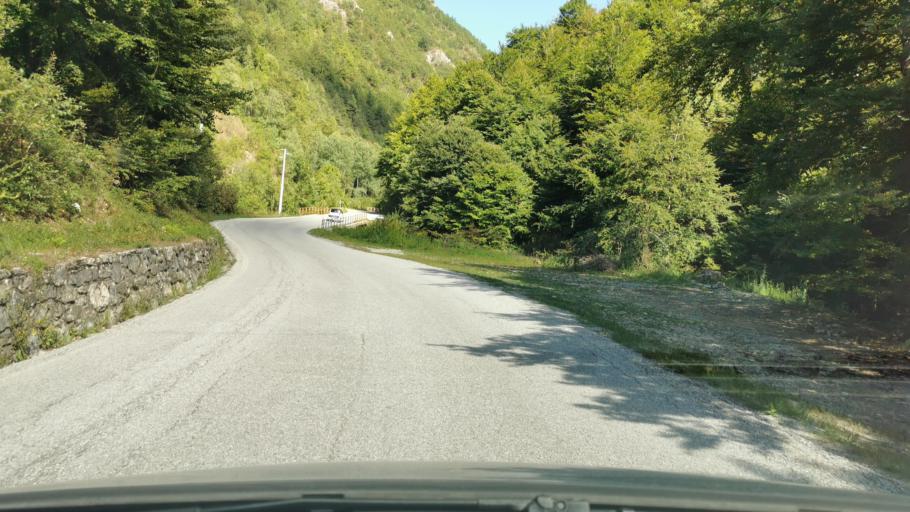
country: IT
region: Piedmont
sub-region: Provincia di Cuneo
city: Campomolino
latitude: 44.4113
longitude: 7.2455
